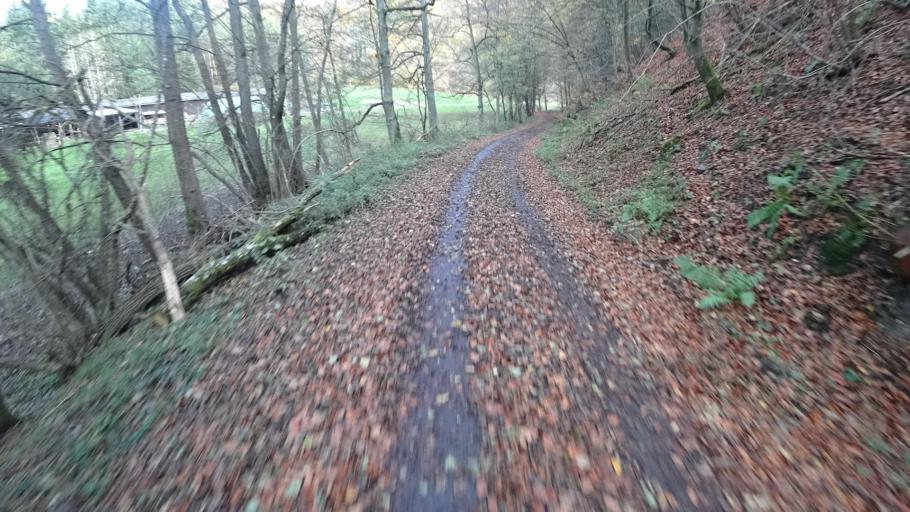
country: DE
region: Rheinland-Pfalz
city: Sierscheid
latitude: 50.4826
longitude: 6.9134
